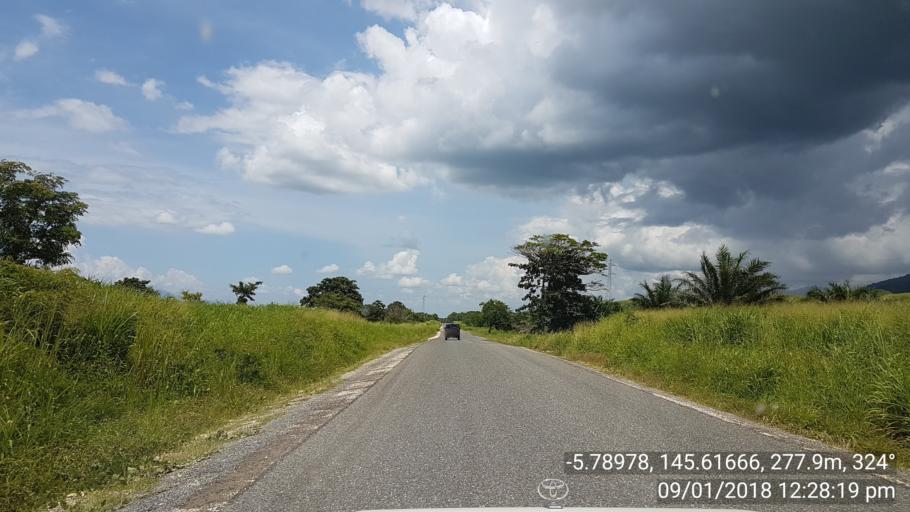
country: PG
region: Eastern Highlands
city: Goroka
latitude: -5.7900
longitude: 145.6170
